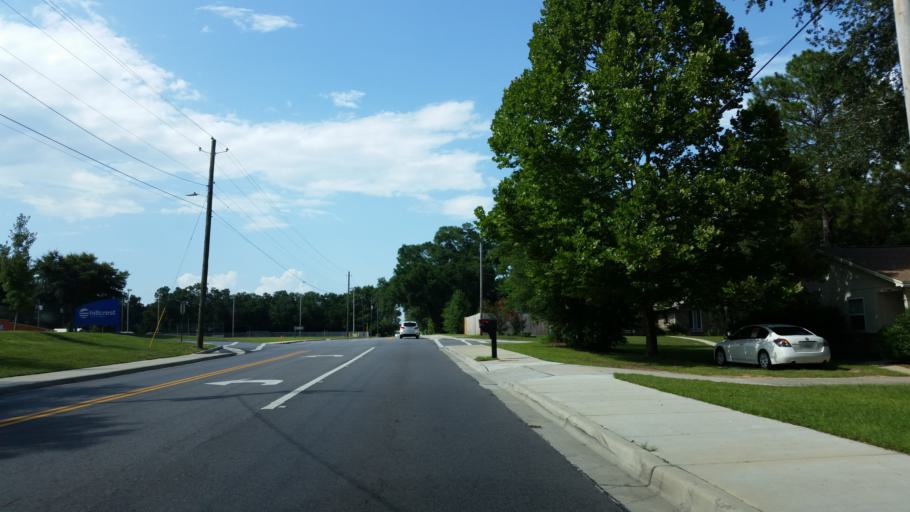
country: US
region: Florida
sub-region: Escambia County
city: Ensley
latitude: 30.5344
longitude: -87.2476
